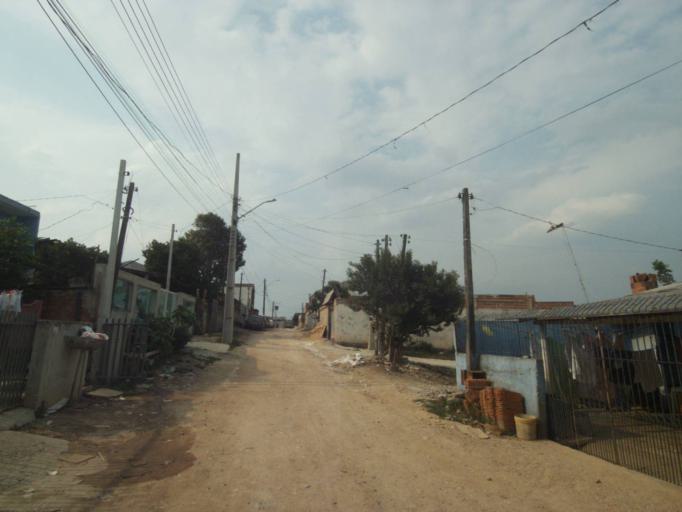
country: BR
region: Parana
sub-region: Sao Jose Dos Pinhais
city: Sao Jose dos Pinhais
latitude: -25.5385
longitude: -49.2322
